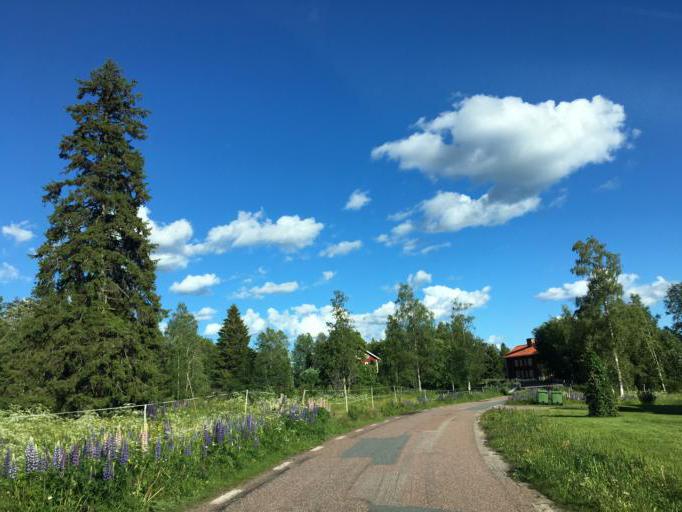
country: SE
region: OErebro
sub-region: Hallefors Kommun
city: Haellefors
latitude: 60.0417
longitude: 14.5195
